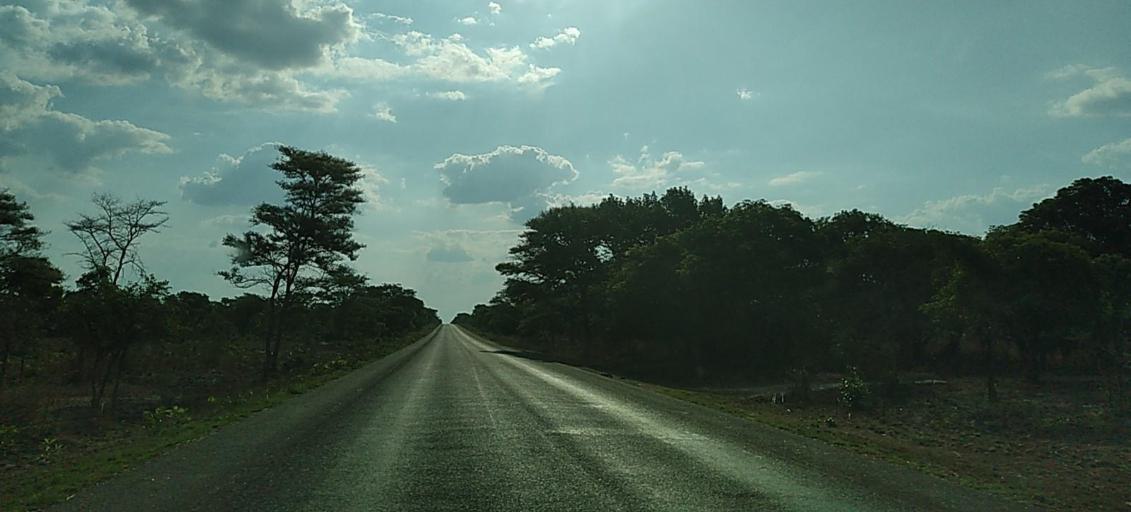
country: ZM
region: Copperbelt
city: Luanshya
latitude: -13.3888
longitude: 28.3814
